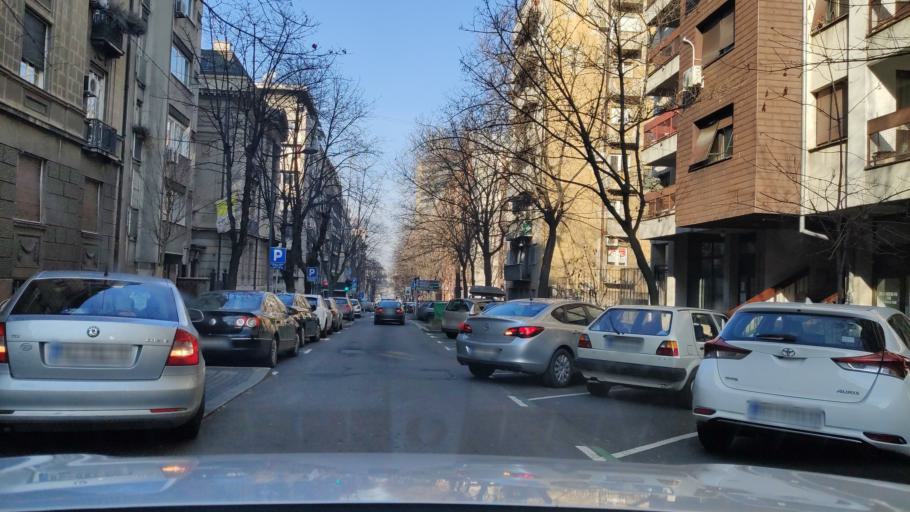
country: RS
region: Central Serbia
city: Belgrade
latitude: 44.7998
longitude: 20.4682
